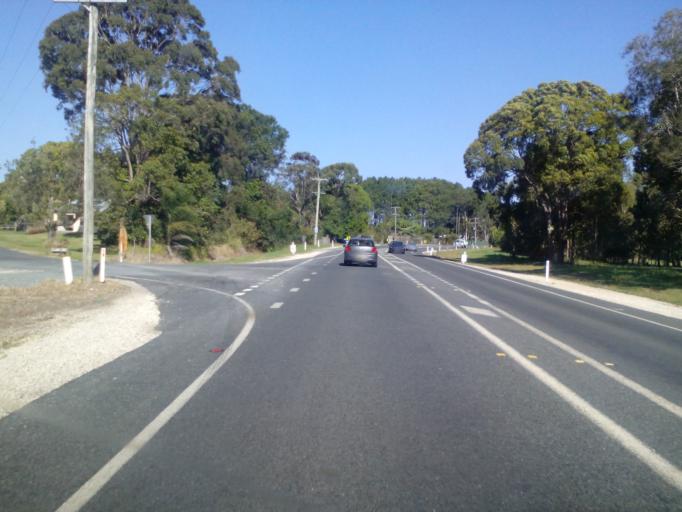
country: AU
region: New South Wales
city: Chinderah
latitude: -28.2516
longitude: 153.5580
